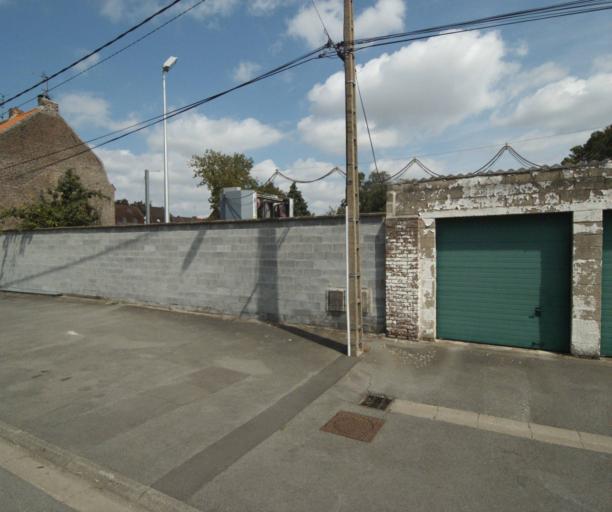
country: FR
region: Nord-Pas-de-Calais
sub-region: Departement du Nord
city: Lannoy
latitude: 50.6624
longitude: 3.2028
